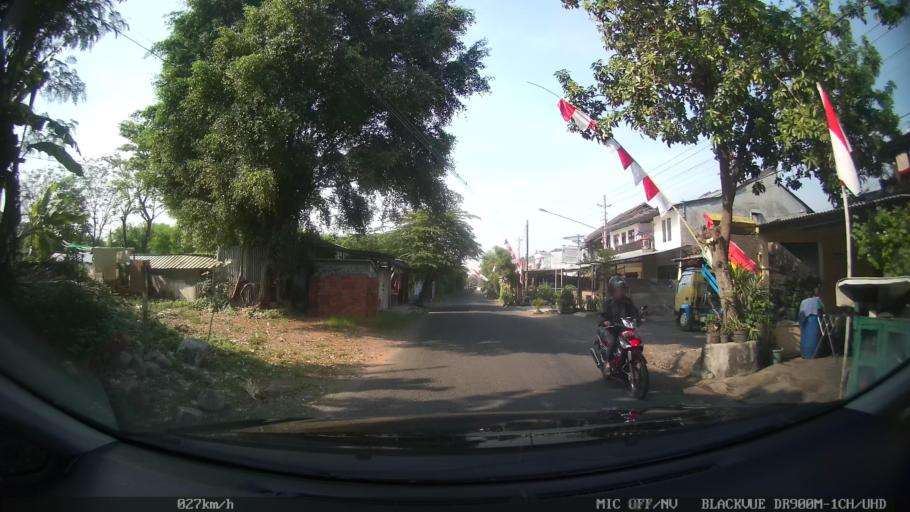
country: ID
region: Daerah Istimewa Yogyakarta
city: Yogyakarta
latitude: -7.7842
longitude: 110.3584
